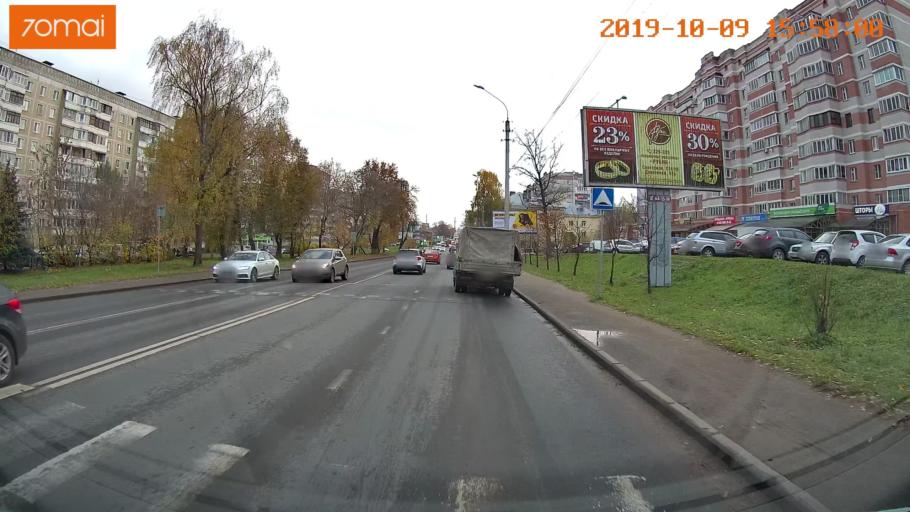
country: RU
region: Kostroma
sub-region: Kostromskoy Rayon
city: Kostroma
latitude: 57.7685
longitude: 40.9508
